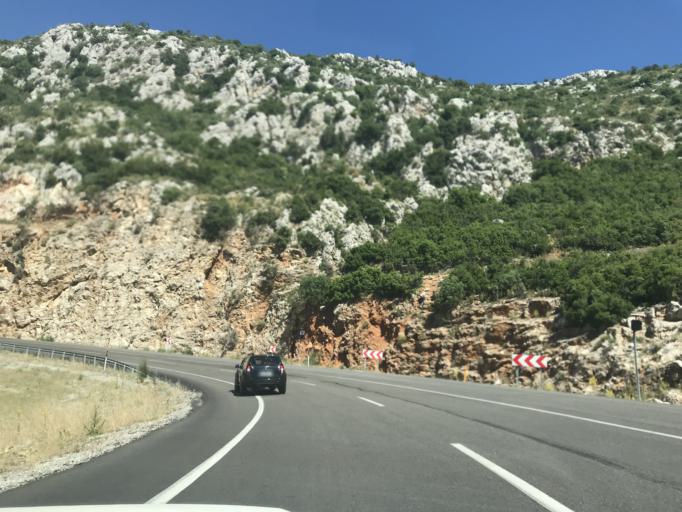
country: TR
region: Antalya
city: Dagbeli
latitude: 37.1644
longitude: 30.5103
